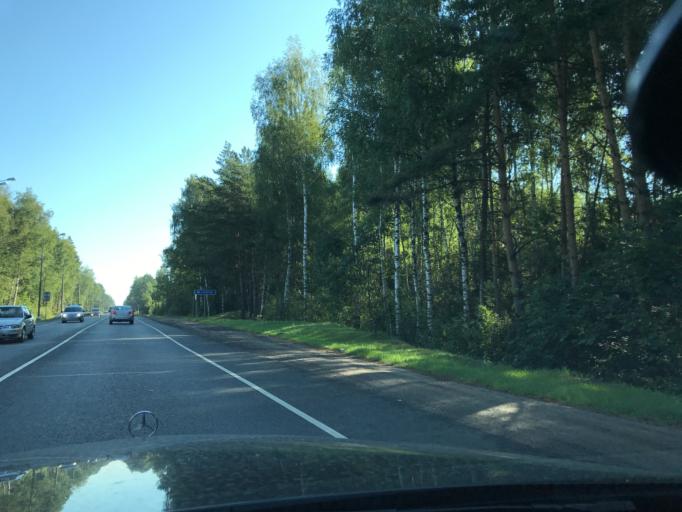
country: RU
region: Moskovskaya
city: Losino-Petrovskiy
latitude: 55.9421
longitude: 38.2213
